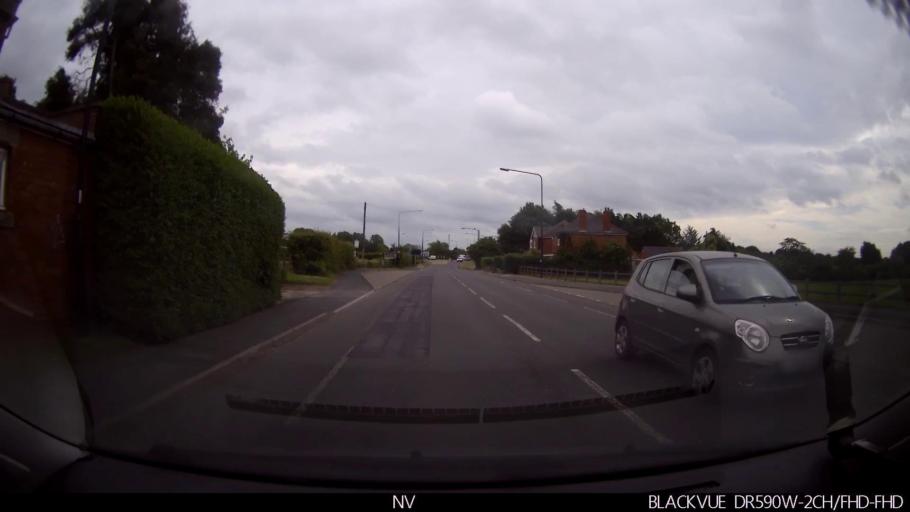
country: GB
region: England
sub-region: City of York
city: Haxby
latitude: 54.0029
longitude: -1.0732
